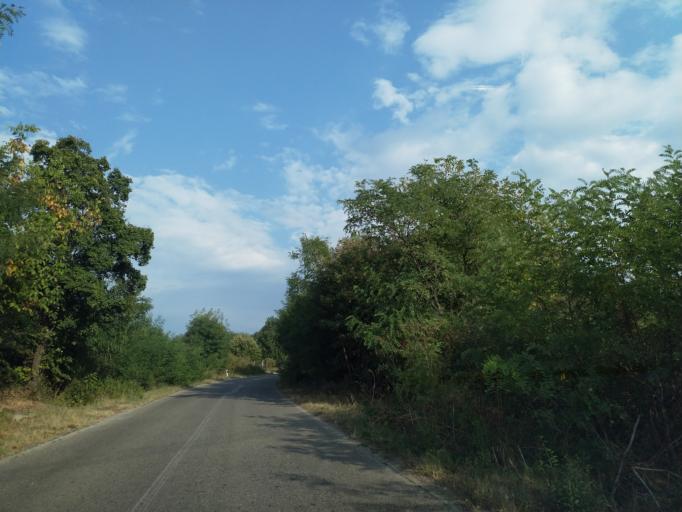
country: RS
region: Central Serbia
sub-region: Pomoravski Okrug
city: Paracin
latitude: 43.8500
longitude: 21.4484
